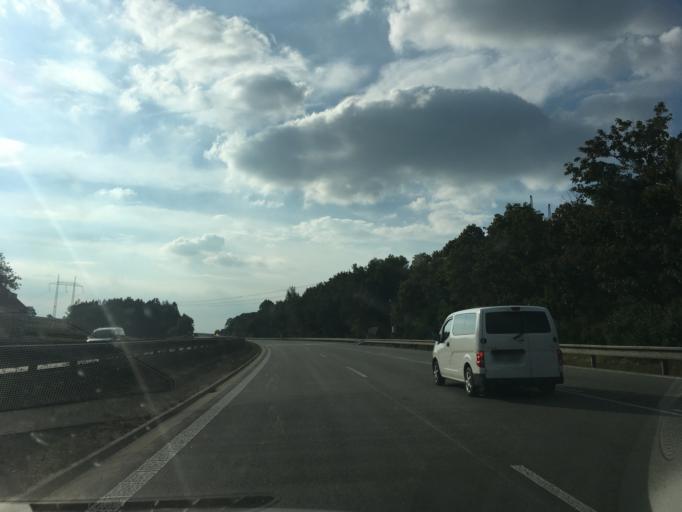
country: CZ
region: Central Bohemia
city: Divisov
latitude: 49.7961
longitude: 14.9215
